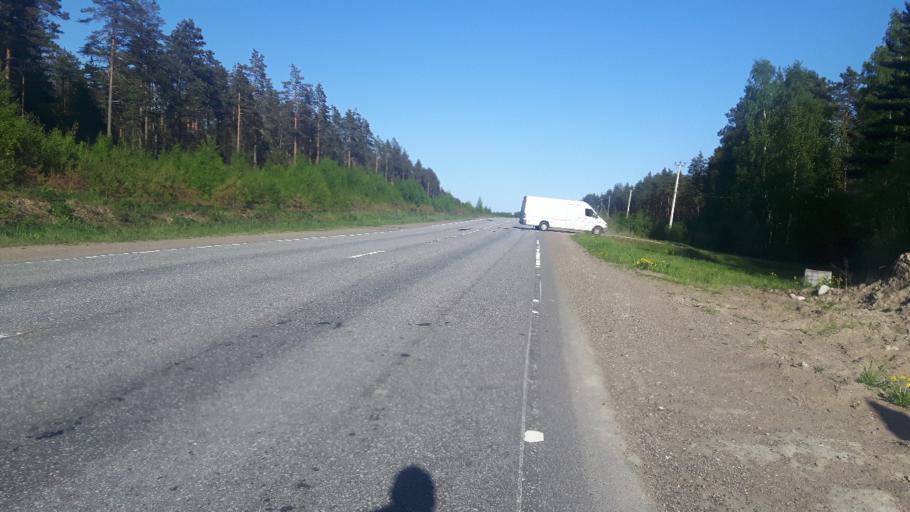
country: RU
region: Leningrad
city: Lebyazh'ye
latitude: 60.1689
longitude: 29.2111
